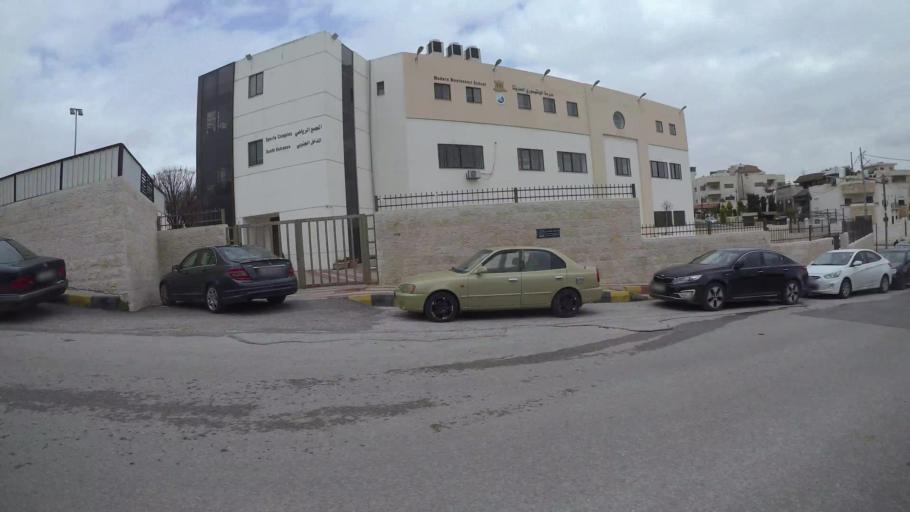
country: JO
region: Amman
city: Wadi as Sir
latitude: 31.9851
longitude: 35.8356
